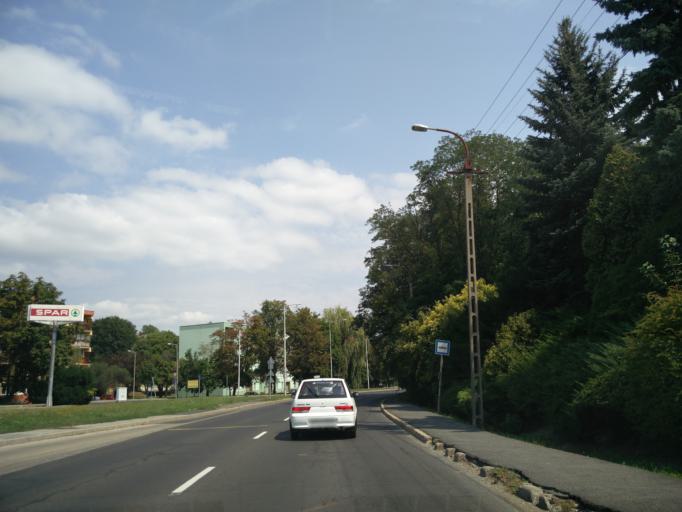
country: HU
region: Zala
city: Zalaegerszeg
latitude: 46.8322
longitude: 16.8280
